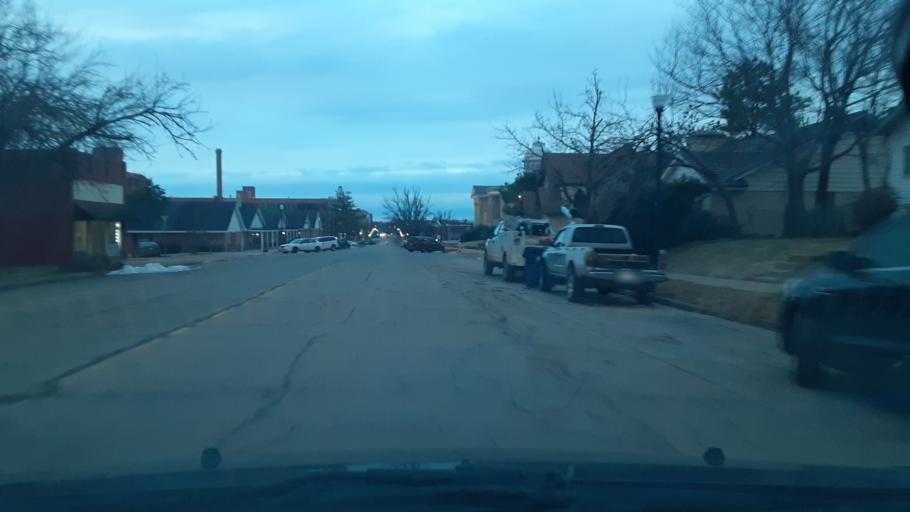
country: US
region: Oklahoma
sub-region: Logan County
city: Guthrie
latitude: 35.8781
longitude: -97.4196
